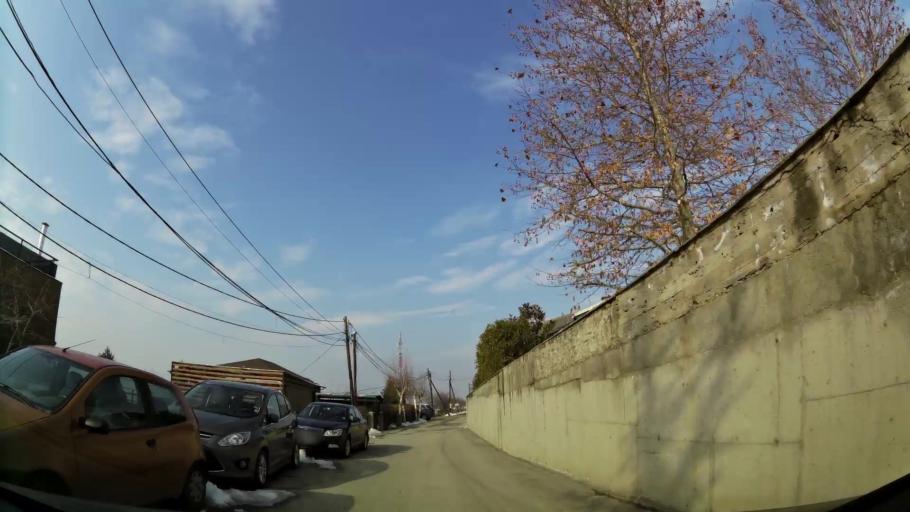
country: MK
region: Suto Orizari
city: Suto Orizare
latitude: 42.0308
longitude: 21.3770
